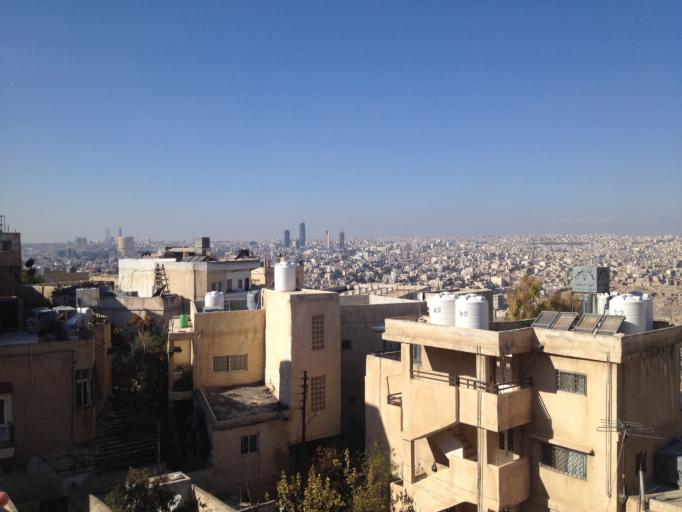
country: JO
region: Amman
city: Amman
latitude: 31.9448
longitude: 35.9413
